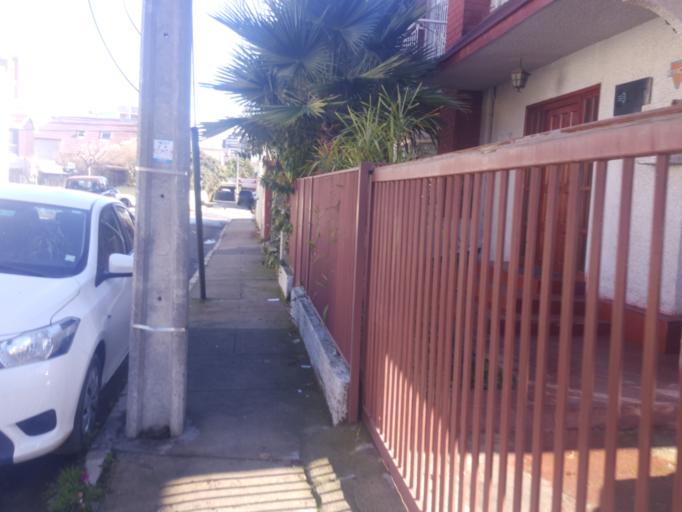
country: CL
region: Valparaiso
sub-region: Provincia de Valparaiso
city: Vina del Mar
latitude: -33.0142
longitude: -71.5465
